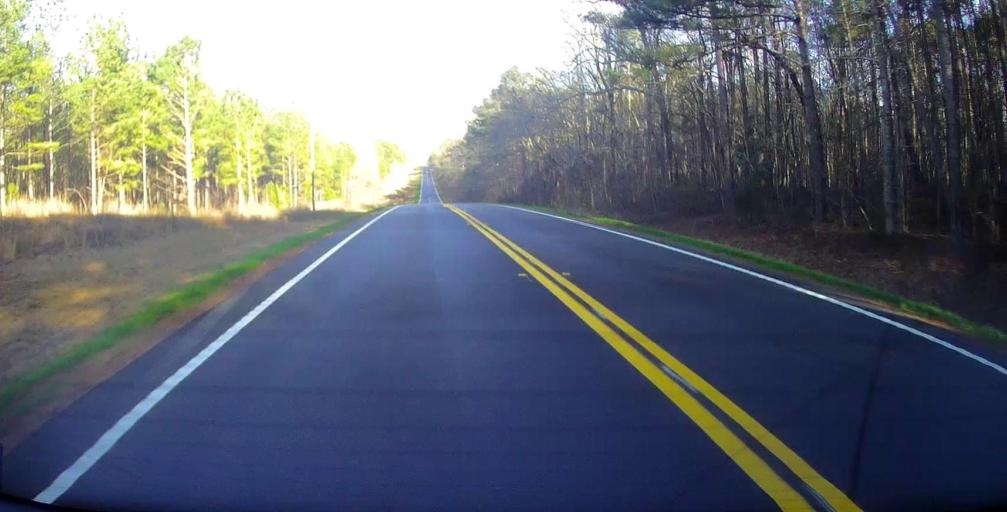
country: US
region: Georgia
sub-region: Harris County
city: Hamilton
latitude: 32.7473
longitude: -84.9991
